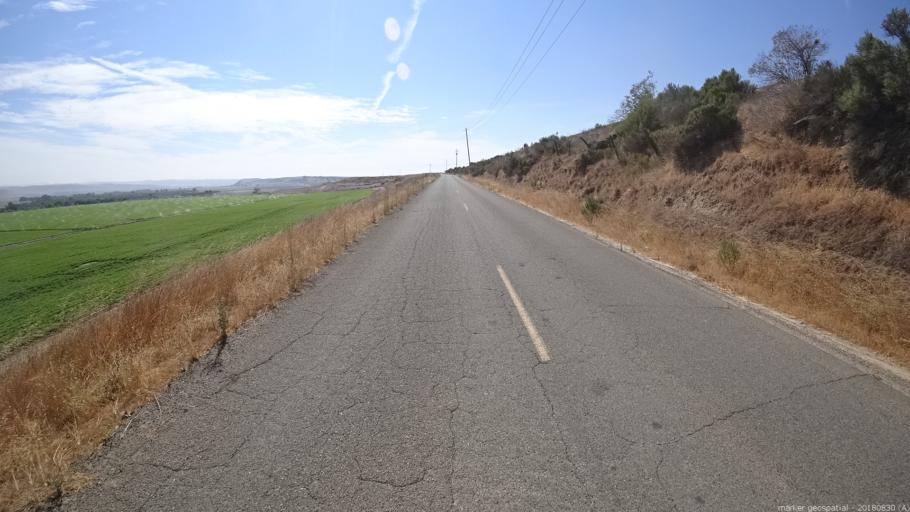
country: US
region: California
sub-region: Monterey County
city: King City
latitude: 36.0986
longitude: -121.0215
